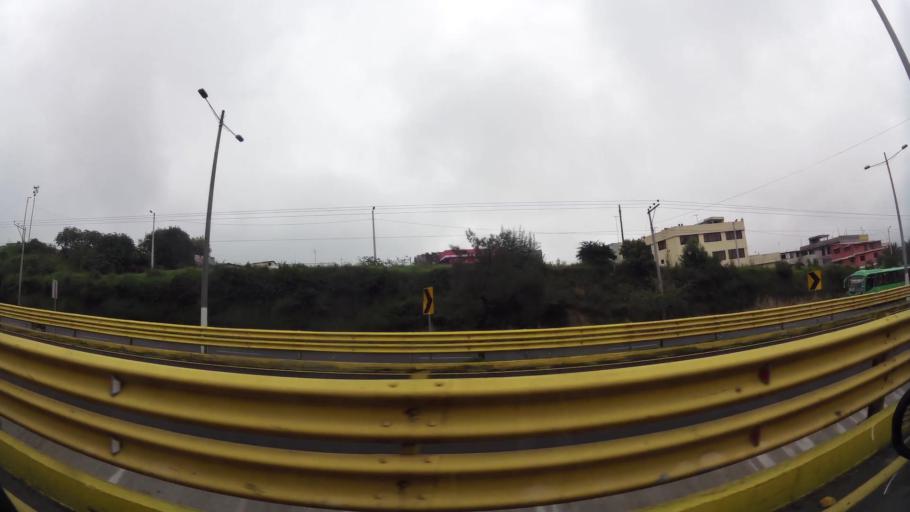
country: EC
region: Pichincha
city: Sangolqui
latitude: -0.2804
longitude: -78.4725
